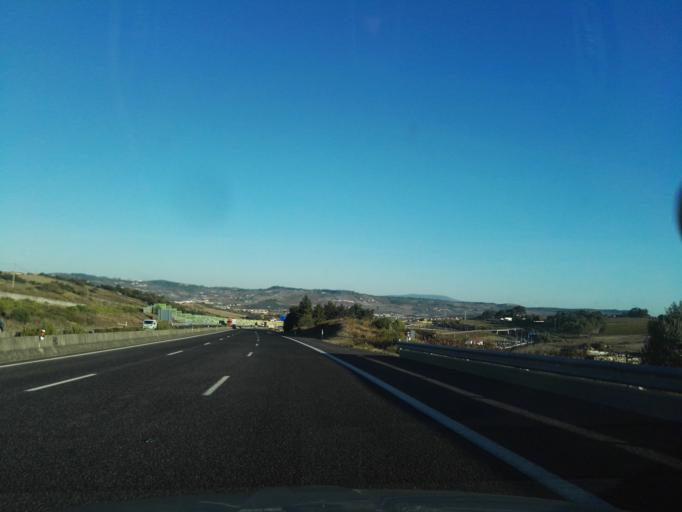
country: PT
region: Lisbon
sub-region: Arruda Dos Vinhos
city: Arruda dos Vinhos
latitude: 38.9591
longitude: -9.0619
